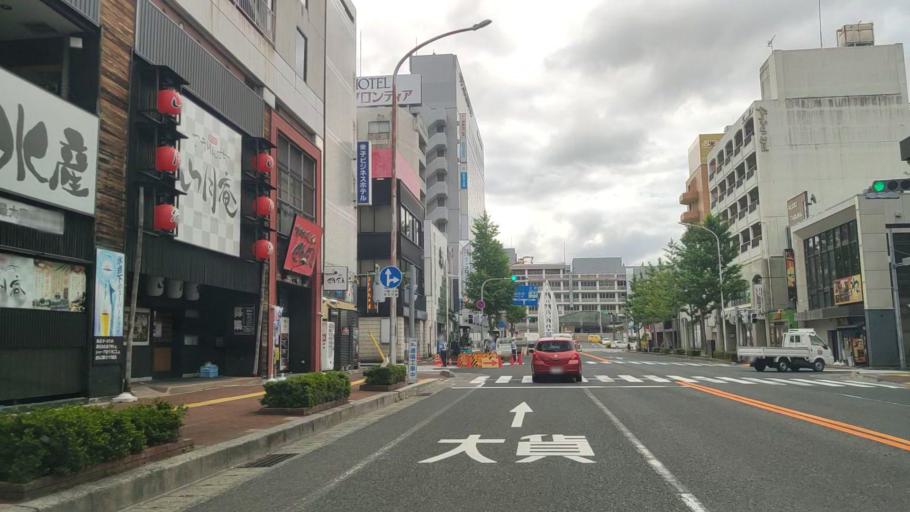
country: JP
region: Tottori
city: Yonago
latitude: 35.4243
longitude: 133.3344
